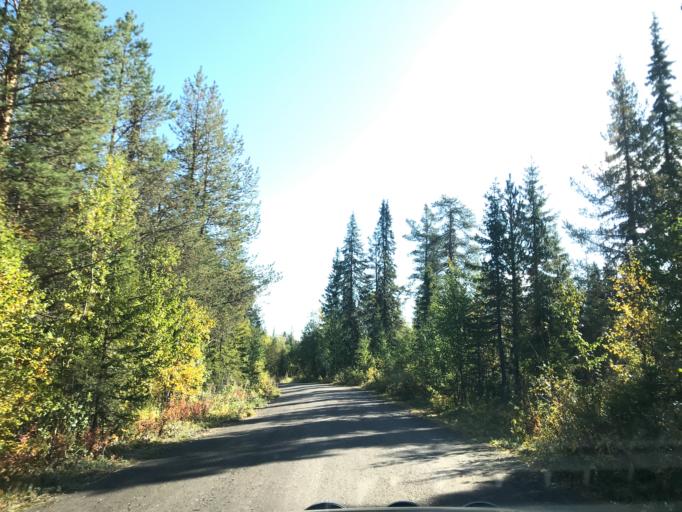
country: SE
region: Norrbotten
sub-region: Gallivare Kommun
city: Malmberget
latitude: 67.6463
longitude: 21.1044
